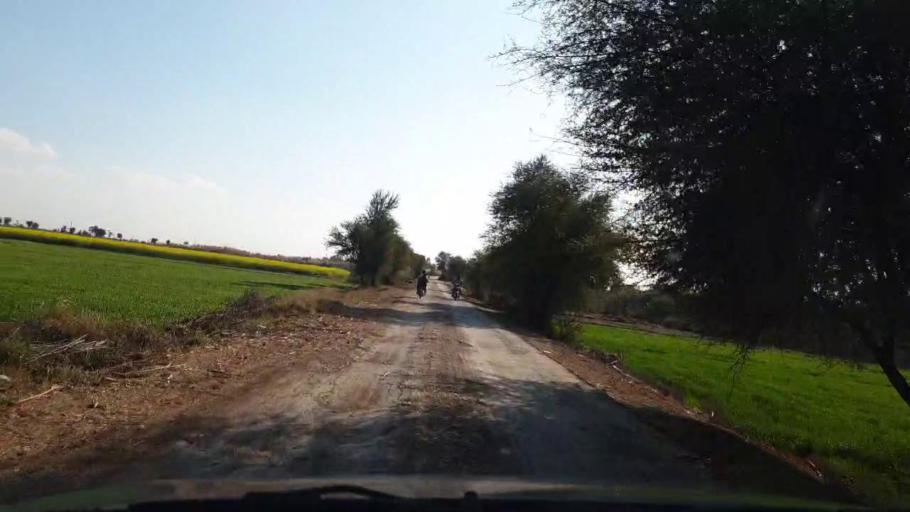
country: PK
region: Sindh
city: Sinjhoro
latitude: 25.9786
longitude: 68.7253
